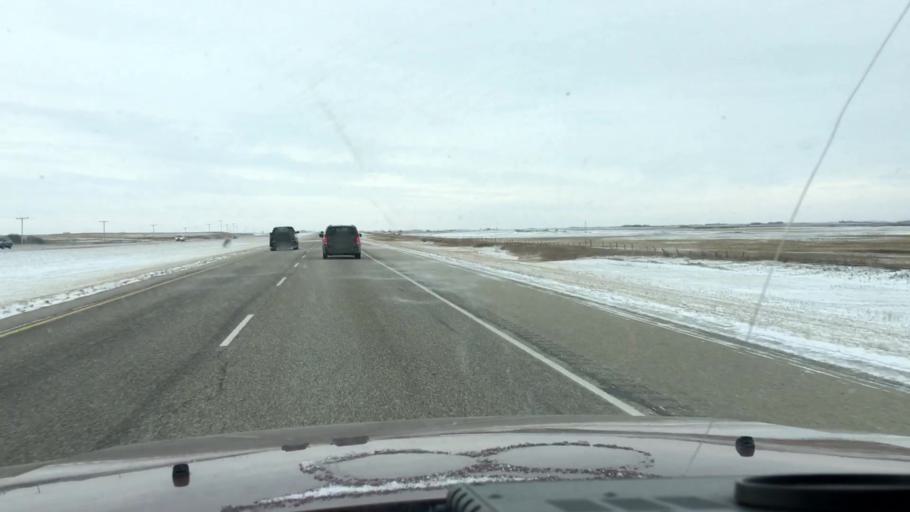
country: CA
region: Saskatchewan
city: Saskatoon
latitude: 51.5969
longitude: -106.3907
